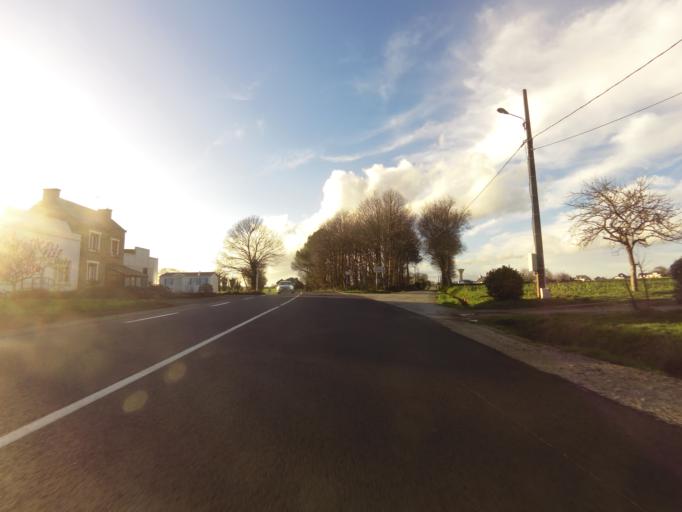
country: FR
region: Brittany
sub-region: Departement du Morbihan
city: Pleugriffet
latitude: 47.9792
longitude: -2.6737
